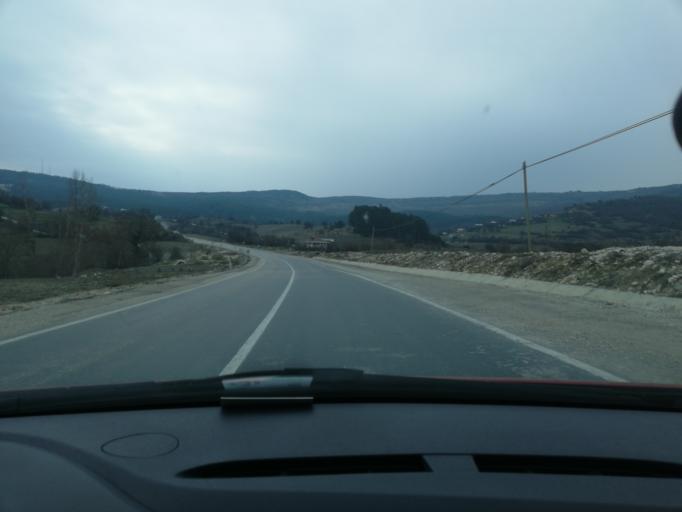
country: TR
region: Kastamonu
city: Pinarbasi
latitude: 41.5885
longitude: 33.0916
